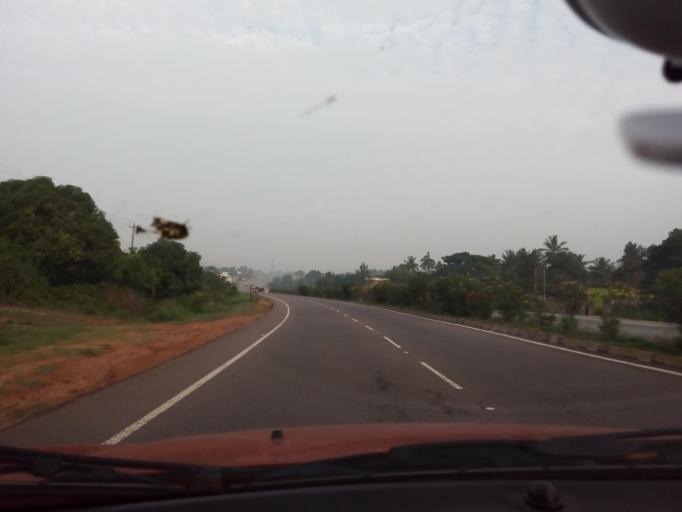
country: IN
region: Karnataka
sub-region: Ramanagara
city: Magadi
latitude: 13.0747
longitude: 77.2162
